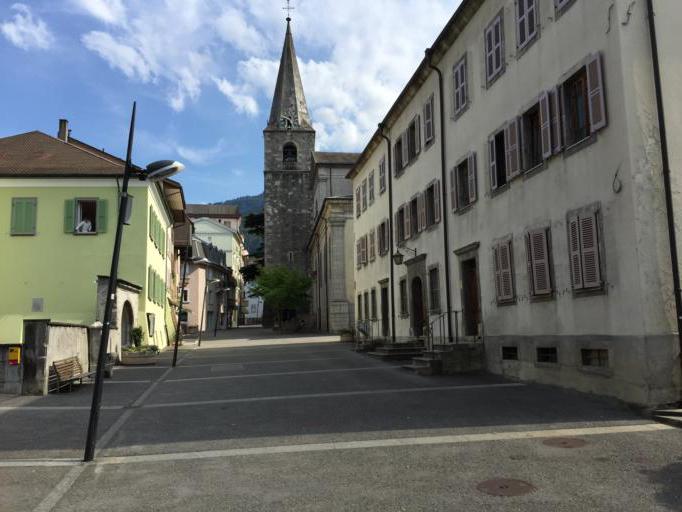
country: CH
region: Valais
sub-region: Monthey District
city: Monthey
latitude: 46.2533
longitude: 6.9469
